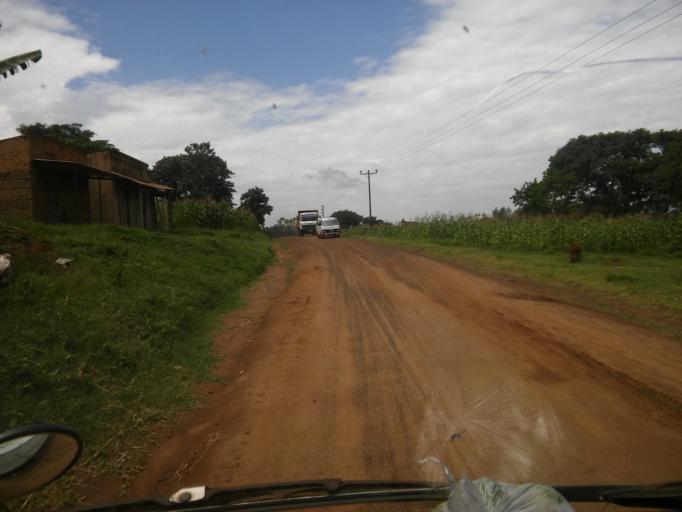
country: KE
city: Malikisi
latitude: 0.8144
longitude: 34.3136
